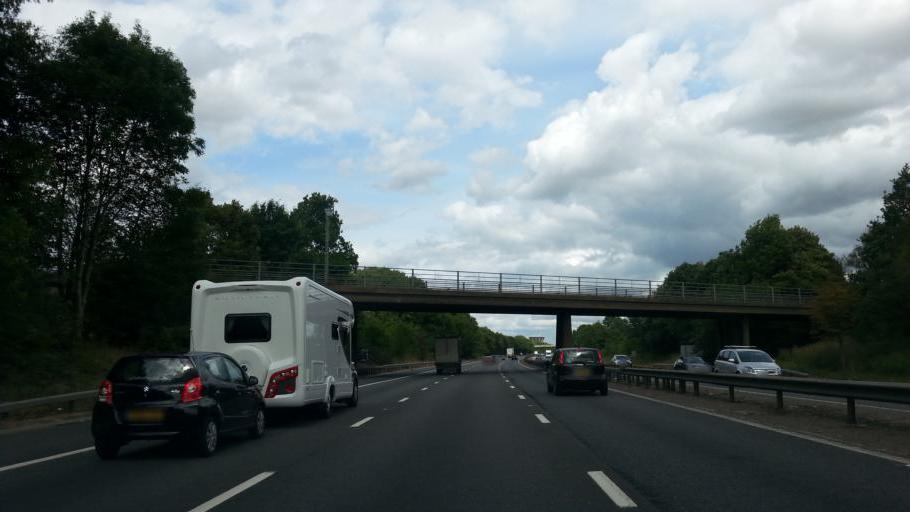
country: GB
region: England
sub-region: Essex
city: Harlow
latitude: 51.7569
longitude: 0.1469
